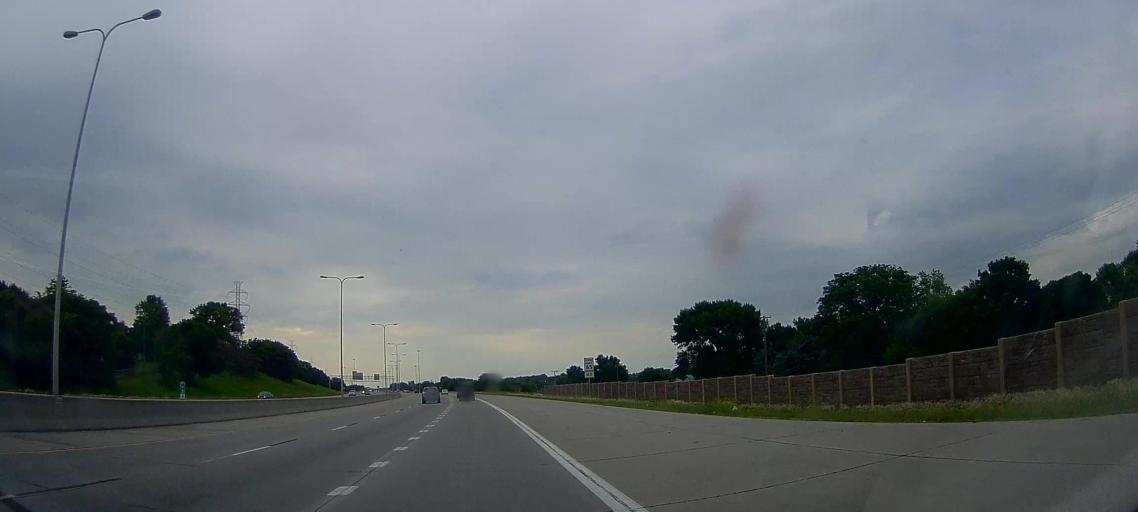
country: US
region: Nebraska
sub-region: Douglas County
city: Ralston
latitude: 41.2975
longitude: -96.0712
